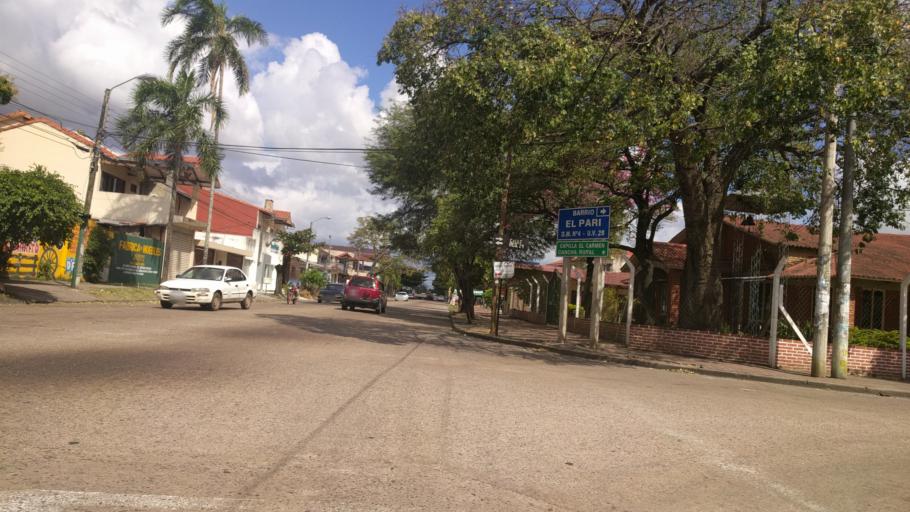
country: BO
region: Santa Cruz
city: Santa Cruz de la Sierra
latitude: -17.8048
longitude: -63.1949
